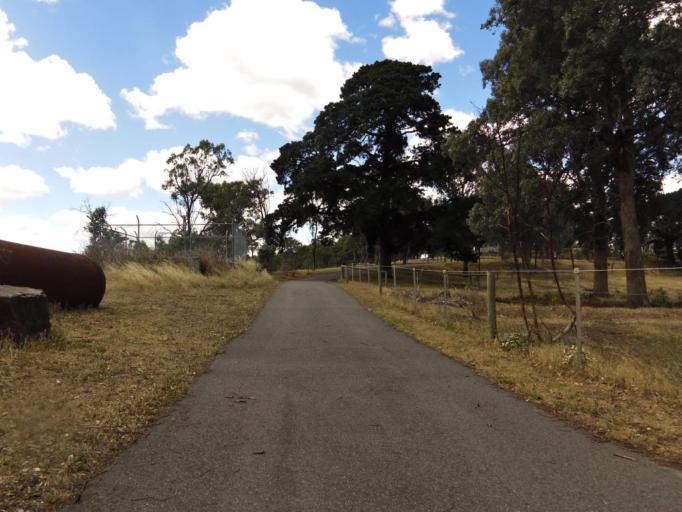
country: AU
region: Victoria
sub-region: Nillumbik
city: Eltham North
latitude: -37.6886
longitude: 145.1645
